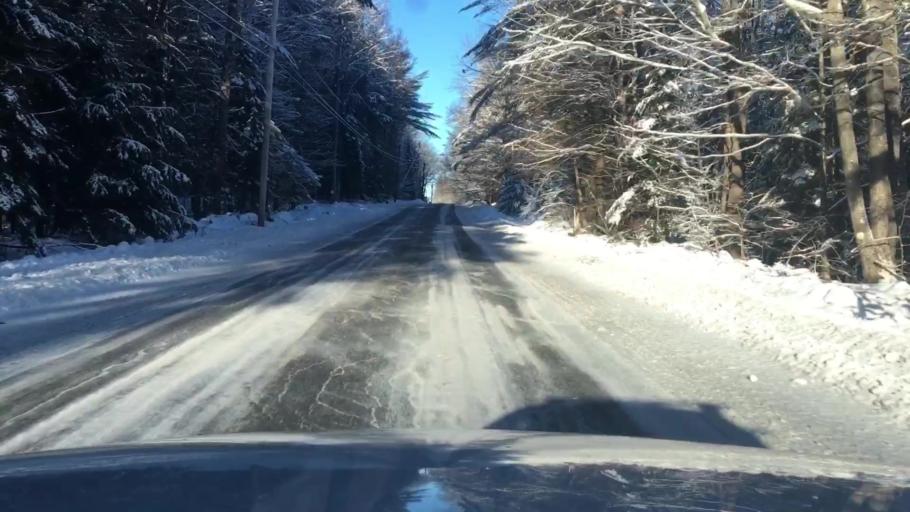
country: US
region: Maine
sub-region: Kennebec County
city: Belgrade
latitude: 44.4206
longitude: -69.8823
